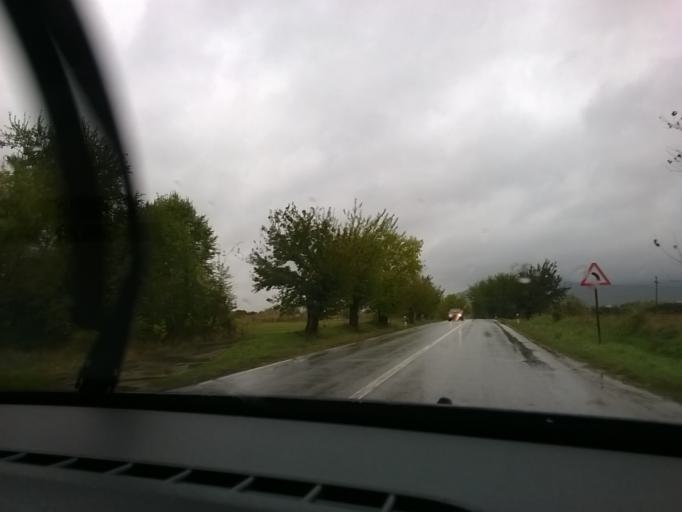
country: RS
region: Autonomna Pokrajina Vojvodina
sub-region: Juznobanatski Okrug
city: Vrsac
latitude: 45.0918
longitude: 21.2999
